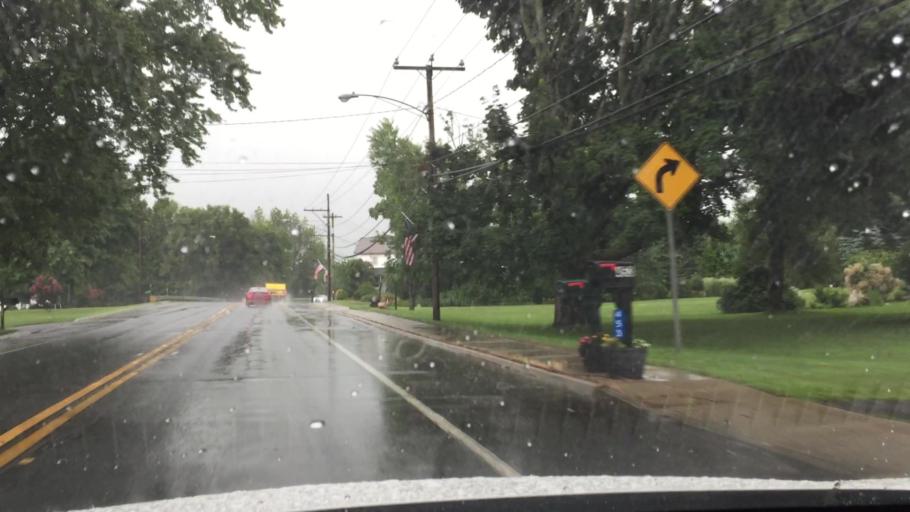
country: US
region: Massachusetts
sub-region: Berkshire County
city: Lanesborough
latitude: 42.5038
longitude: -73.2370
